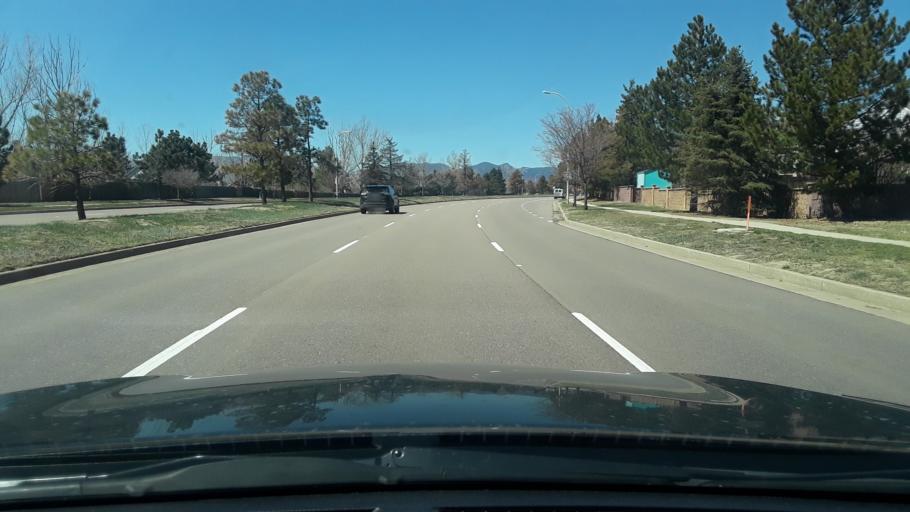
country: US
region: Colorado
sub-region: El Paso County
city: Black Forest
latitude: 38.9548
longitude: -104.7441
